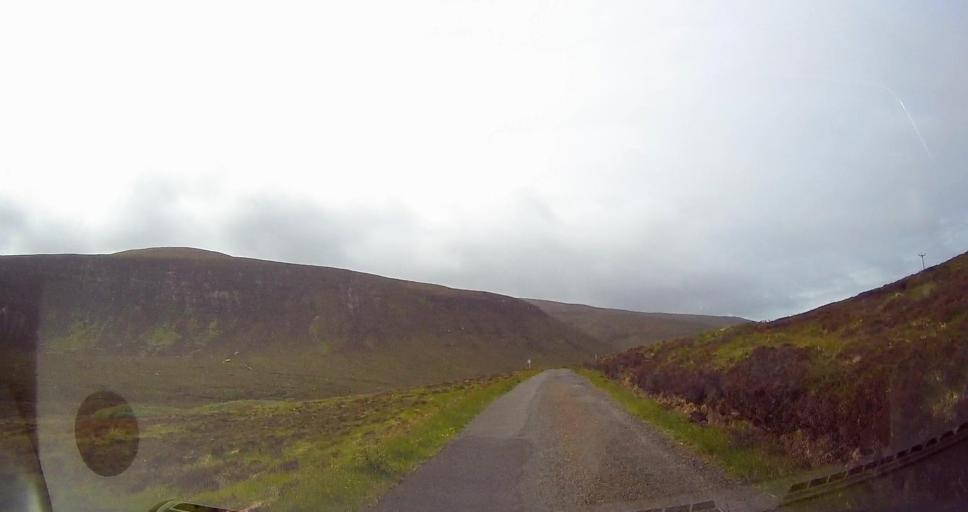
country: GB
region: Scotland
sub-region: Orkney Islands
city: Stromness
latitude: 58.8899
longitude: -3.3154
